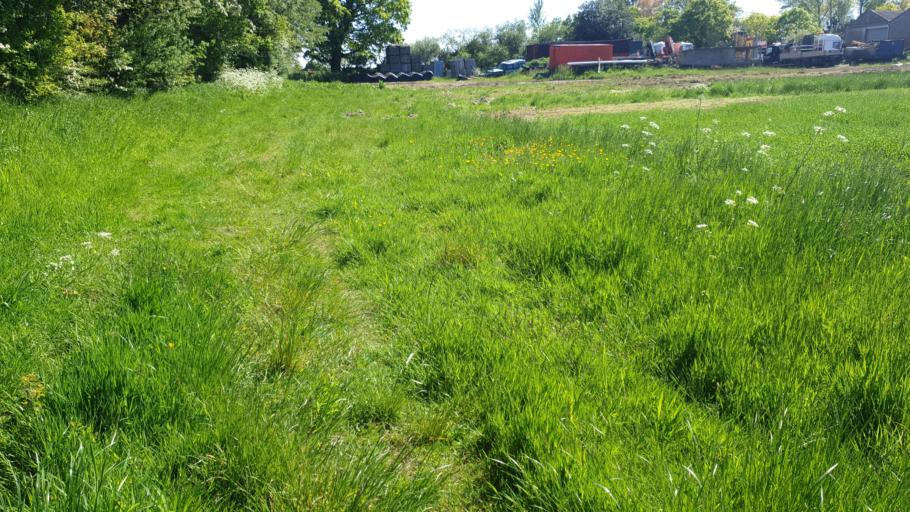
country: GB
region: England
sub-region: Essex
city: Great Bentley
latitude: 51.8582
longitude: 1.0515
